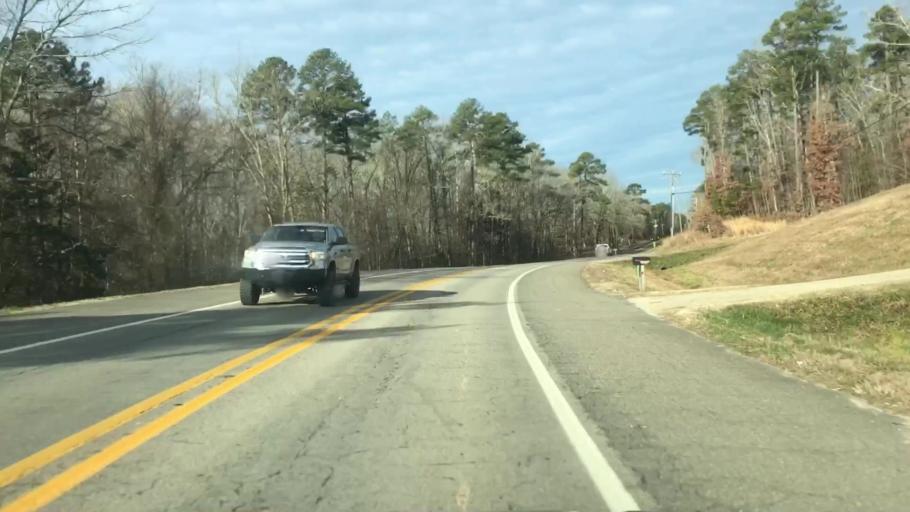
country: US
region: Arkansas
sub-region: Montgomery County
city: Mount Ida
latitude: 34.5393
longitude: -93.6031
